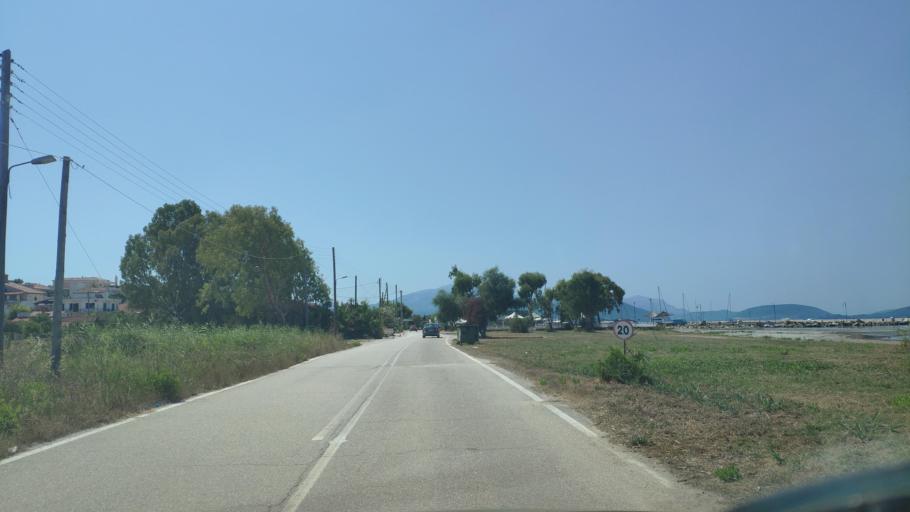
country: GR
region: Epirus
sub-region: Nomos Artas
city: Aneza
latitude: 39.0175
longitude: 20.9136
